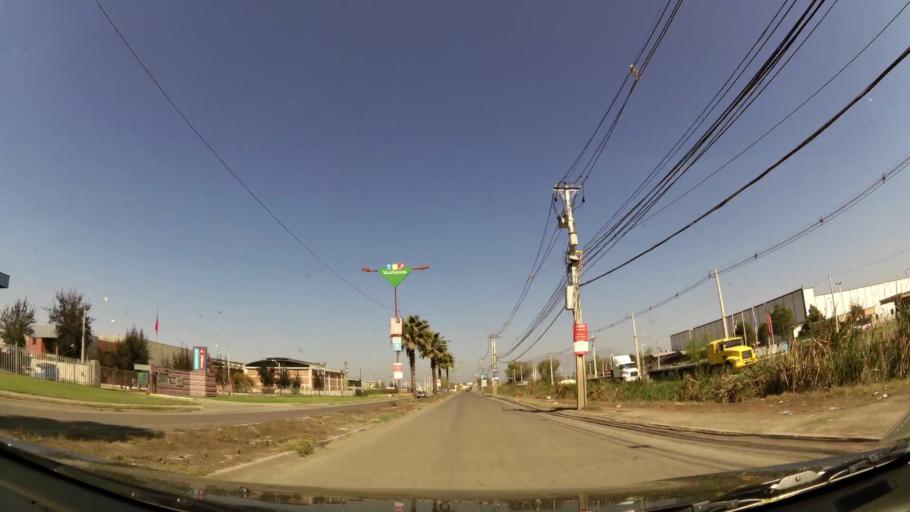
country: CL
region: Santiago Metropolitan
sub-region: Provincia de Chacabuco
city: Chicureo Abajo
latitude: -33.3224
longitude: -70.7390
